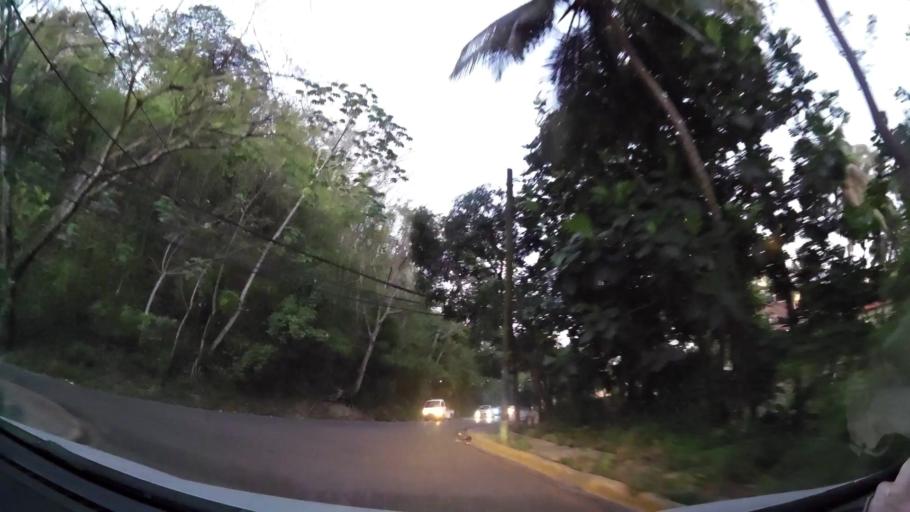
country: DO
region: Nacional
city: La Agustina
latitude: 18.5058
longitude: -69.9472
